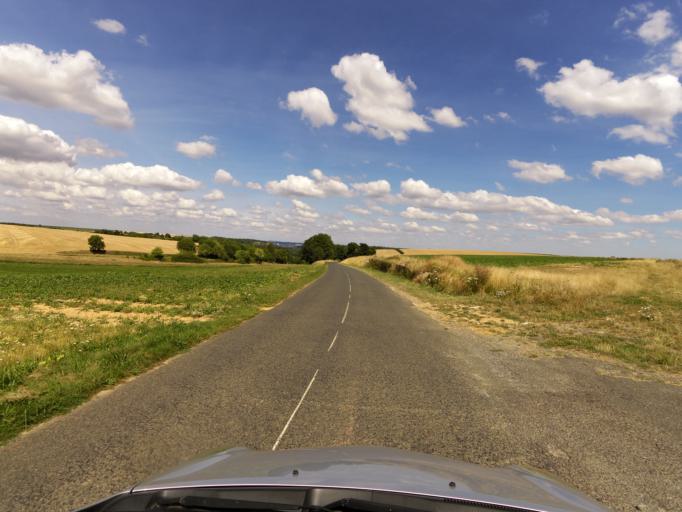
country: FR
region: Picardie
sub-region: Departement de l'Aisne
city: Courmelles
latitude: 49.3259
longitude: 3.2831
